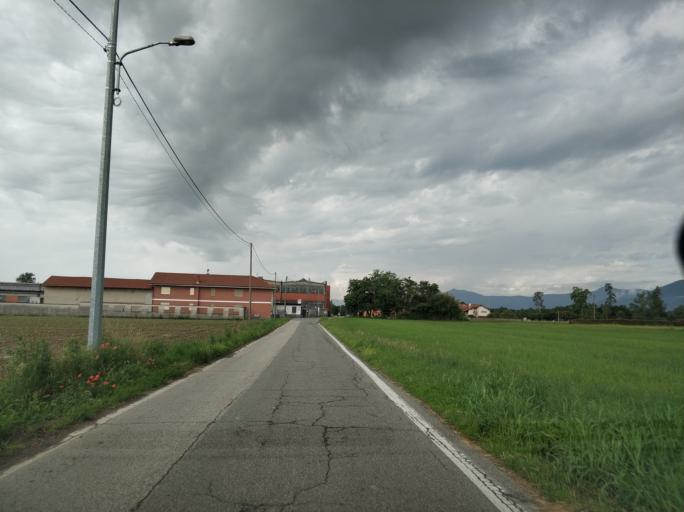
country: IT
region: Piedmont
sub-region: Provincia di Torino
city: San Maurizio
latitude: 45.1991
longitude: 7.6131
